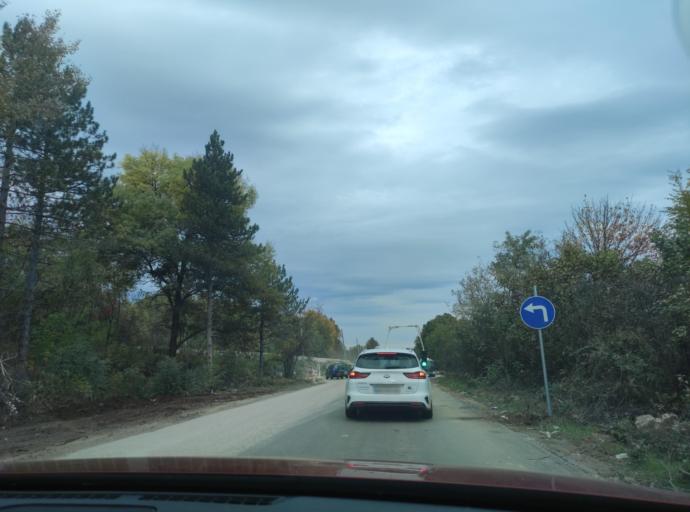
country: BG
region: Montana
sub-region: Obshtina Montana
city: Montana
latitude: 43.3828
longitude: 23.2428
